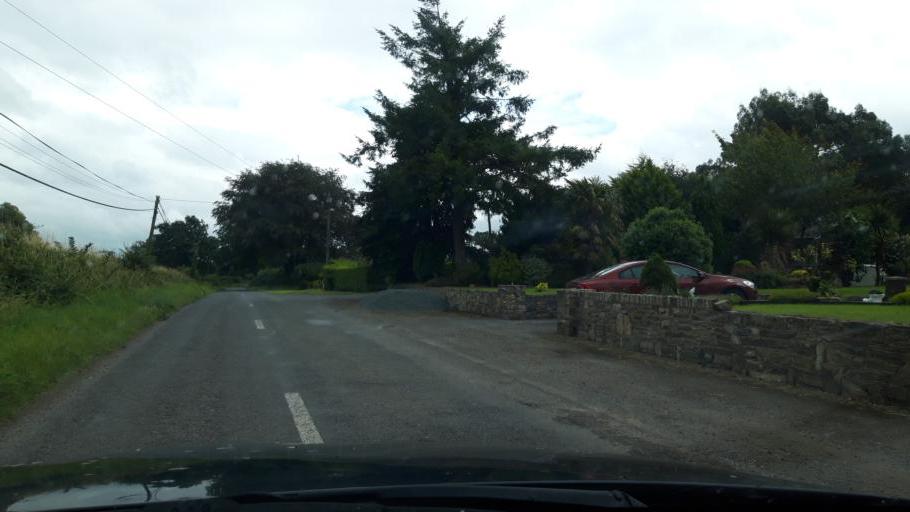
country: IE
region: Munster
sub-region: County Cork
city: Castlemartyr
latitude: 52.1353
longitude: -8.0295
